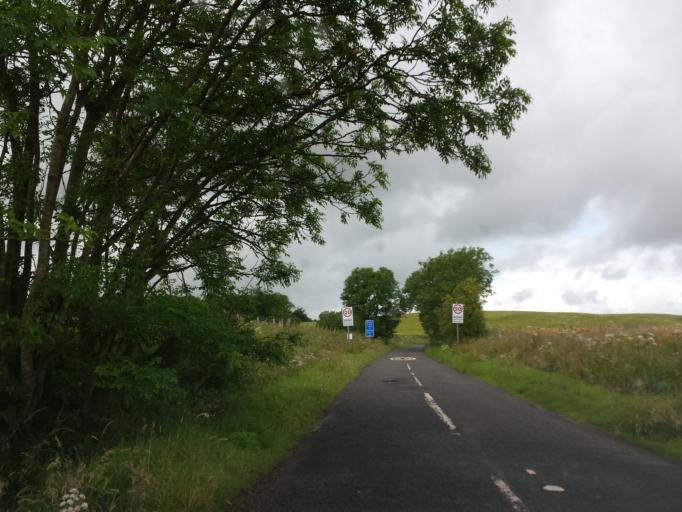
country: GB
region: Scotland
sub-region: Fife
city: Strathkinness
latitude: 56.3566
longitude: -2.8603
